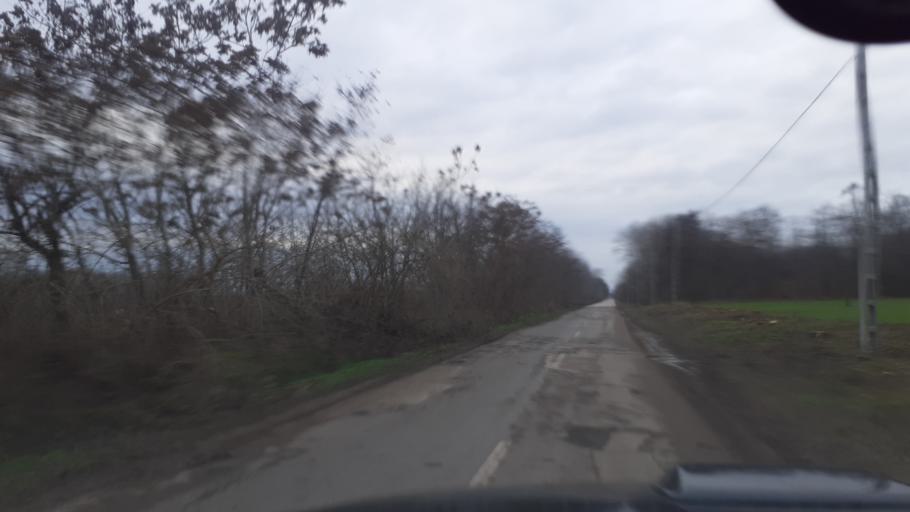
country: HU
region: Bacs-Kiskun
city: Szalkszentmarton
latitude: 46.9482
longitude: 19.0665
